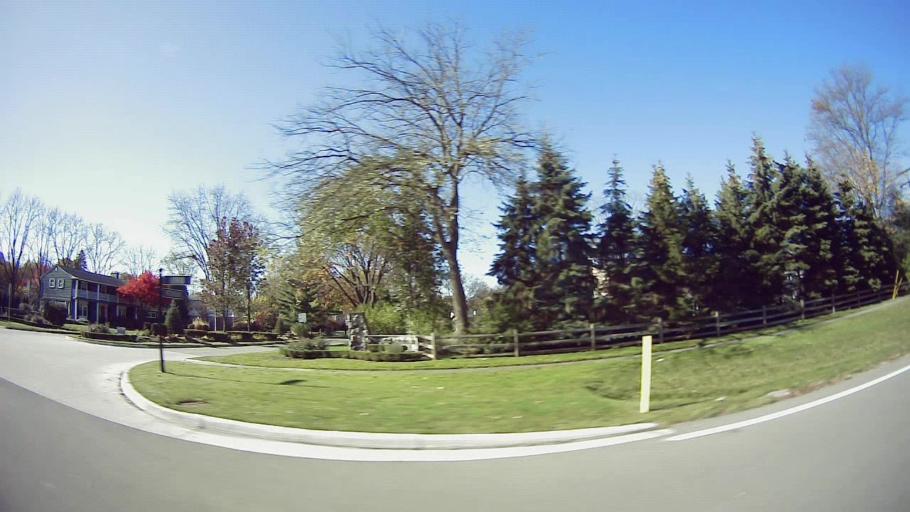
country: US
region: Michigan
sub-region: Oakland County
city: Bingham Farms
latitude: 42.5229
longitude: -83.2635
